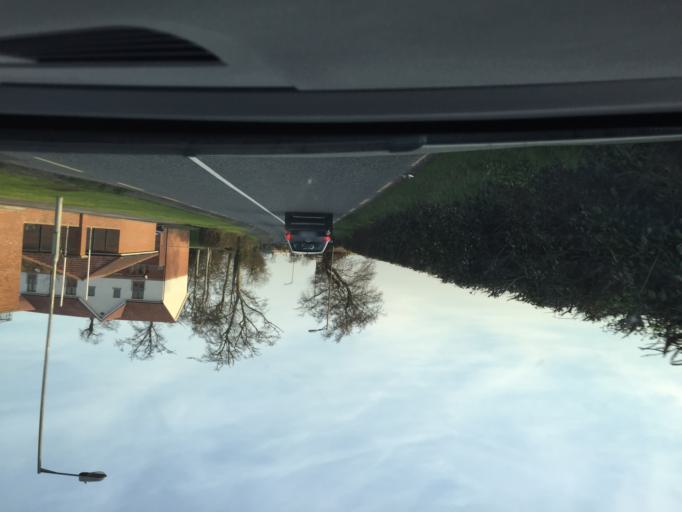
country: IE
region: Leinster
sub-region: An Mhi
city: Dunboyne
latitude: 53.4070
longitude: -6.4456
